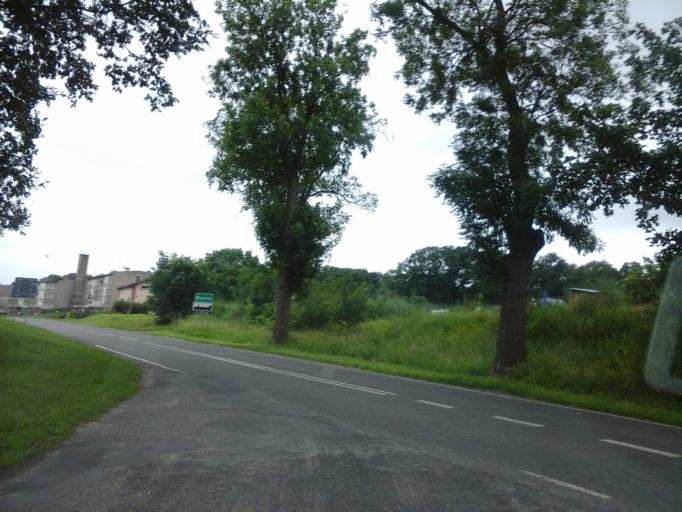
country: PL
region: West Pomeranian Voivodeship
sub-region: Powiat stargardzki
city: Dolice
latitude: 53.1199
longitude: 15.2531
